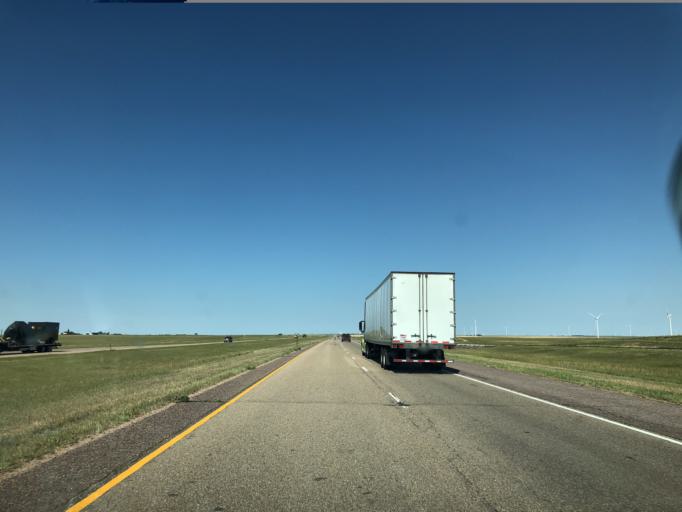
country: US
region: Colorado
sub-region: Lincoln County
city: Hugo
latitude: 39.2806
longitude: -103.3596
